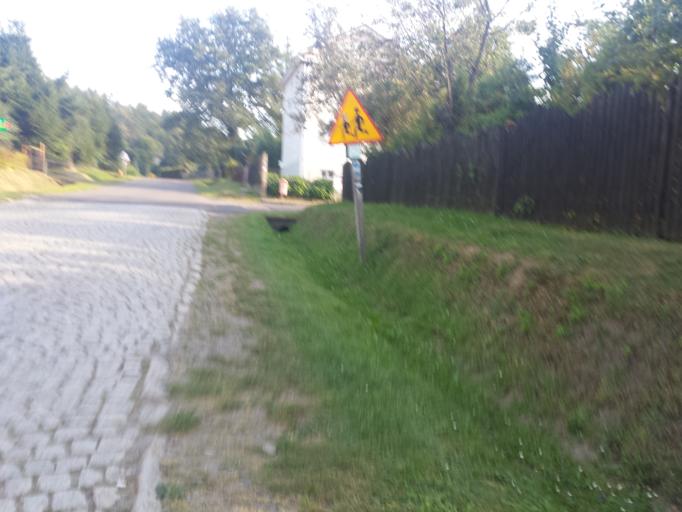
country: PL
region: Subcarpathian Voivodeship
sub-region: Powiat leski
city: Uherce Mineralne
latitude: 49.4350
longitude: 22.4114
